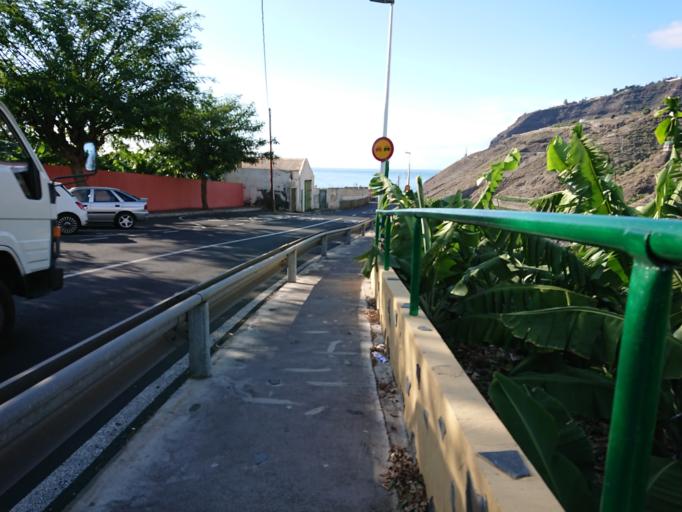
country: ES
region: Canary Islands
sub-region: Provincia de Santa Cruz de Tenerife
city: Tazacorte
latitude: 28.6453
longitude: -17.9352
